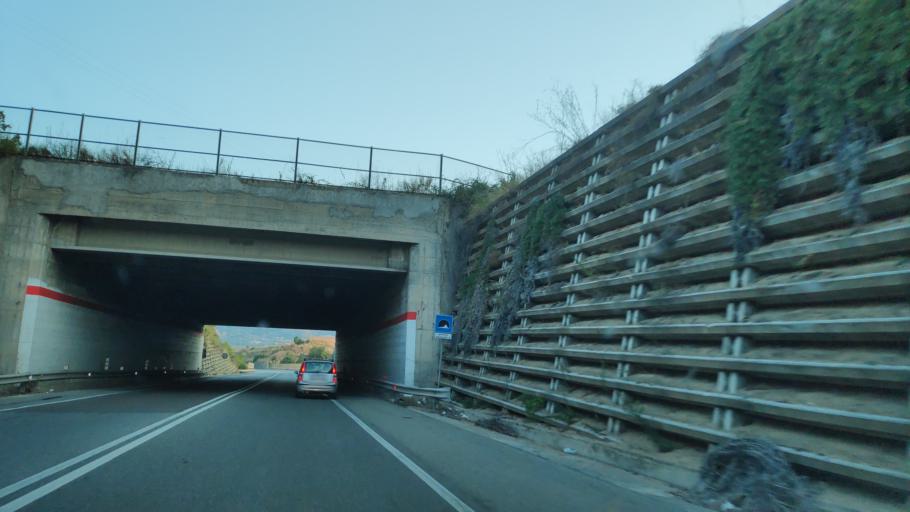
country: IT
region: Calabria
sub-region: Provincia di Catanzaro
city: Soverato Superiore
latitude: 38.6958
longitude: 16.5382
